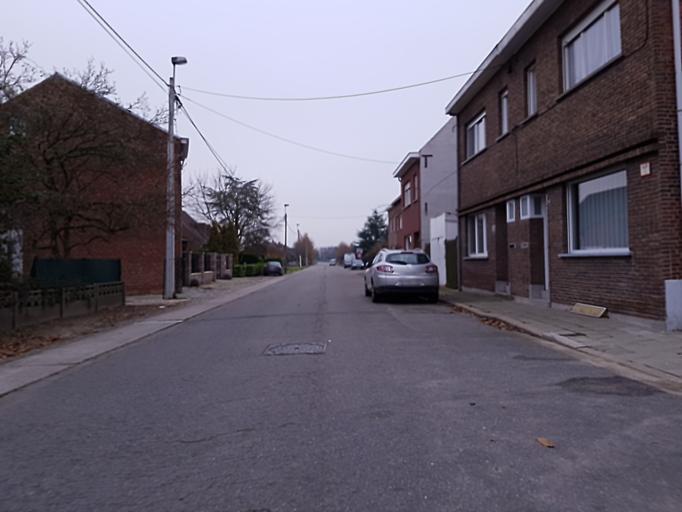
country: BE
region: Flanders
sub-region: Provincie Antwerpen
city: Willebroek
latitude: 51.0458
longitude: 4.3829
